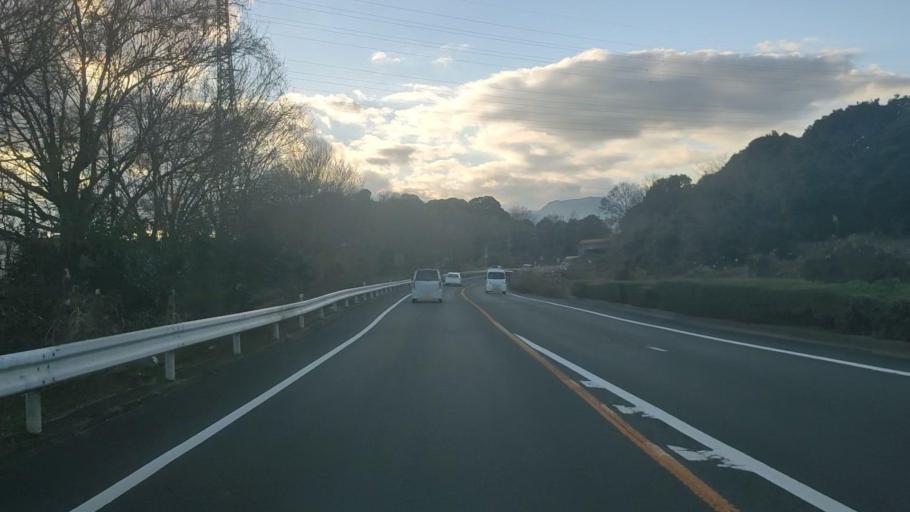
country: JP
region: Saga Prefecture
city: Takeocho-takeo
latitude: 33.2880
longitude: 130.1365
